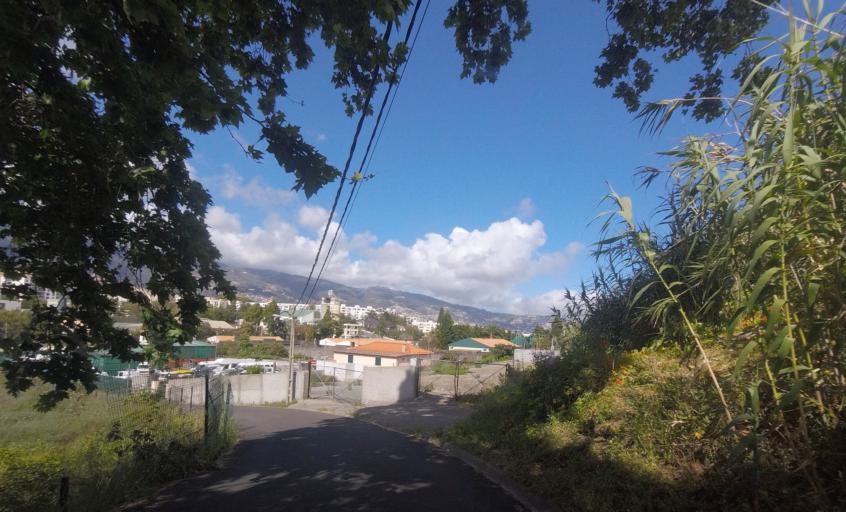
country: PT
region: Madeira
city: Camara de Lobos
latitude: 32.6440
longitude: -16.9401
